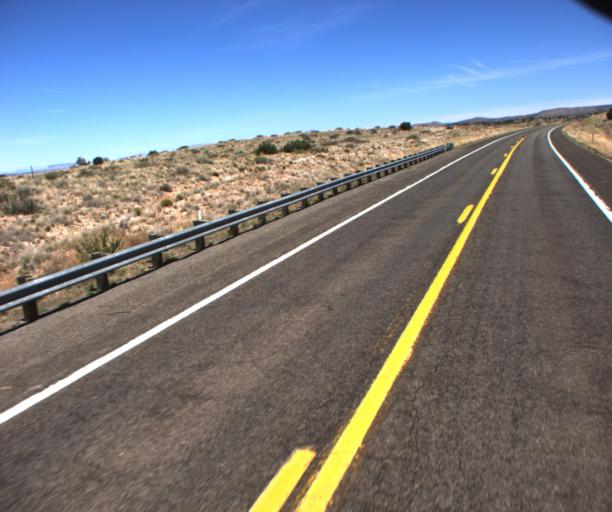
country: US
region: Arizona
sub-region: Mohave County
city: Peach Springs
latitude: 35.5212
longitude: -113.4881
